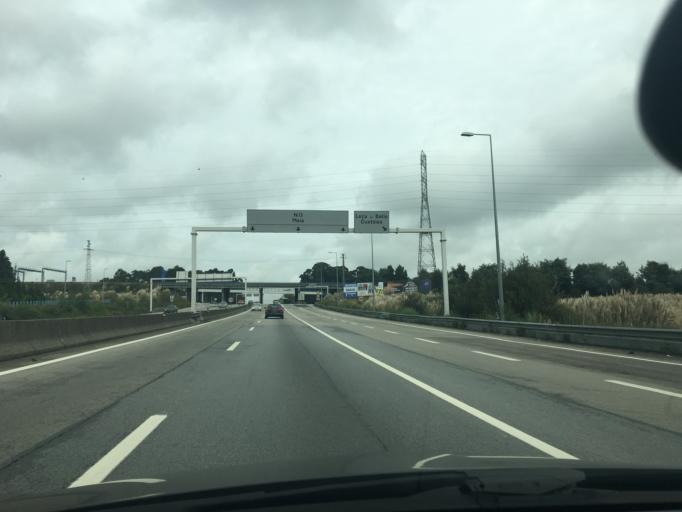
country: PT
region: Porto
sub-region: Maia
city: Leca do Bailio
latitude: 41.2042
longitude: -8.6273
